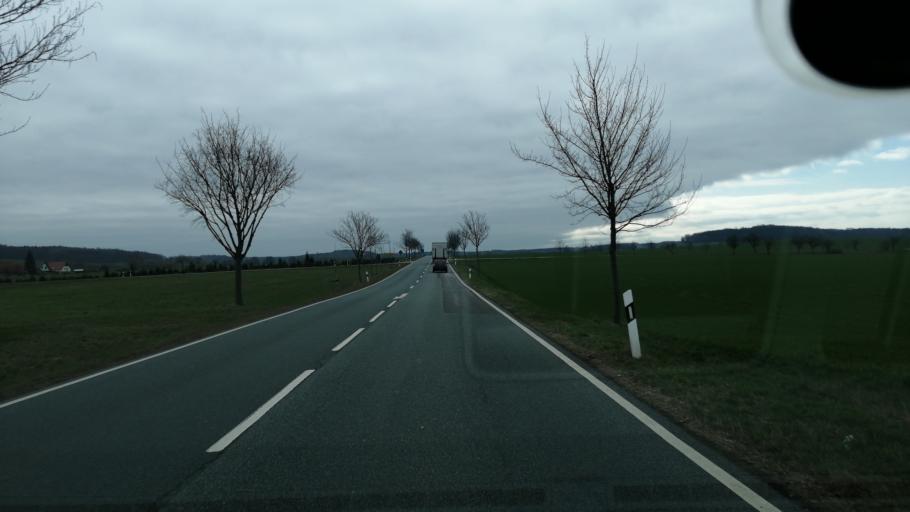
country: DE
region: Saxony
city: Lobau
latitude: 51.0738
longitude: 14.6808
